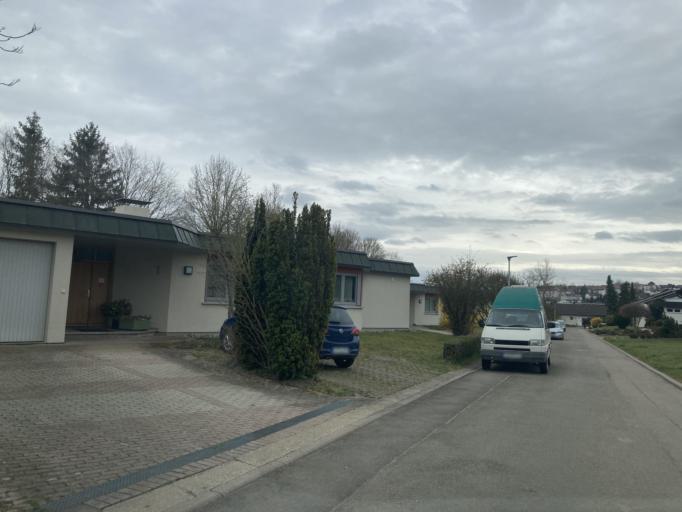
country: DE
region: Baden-Wuerttemberg
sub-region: Tuebingen Region
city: Rottenburg
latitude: 48.4828
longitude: 8.9345
